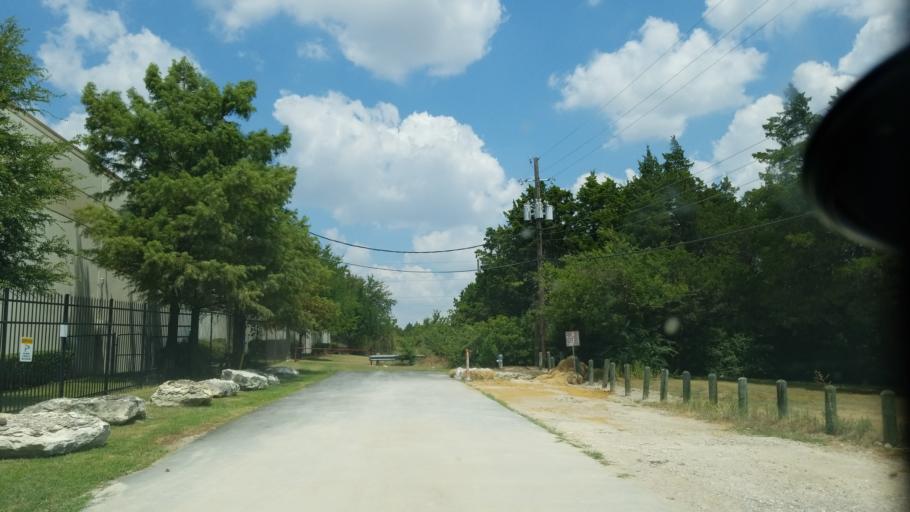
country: US
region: Texas
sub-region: Dallas County
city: Duncanville
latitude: 32.6776
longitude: -96.8881
